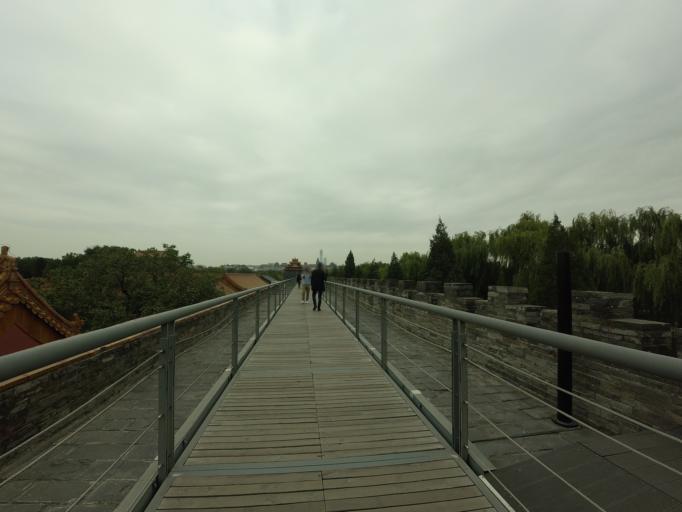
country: CN
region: Beijing
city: Beijing
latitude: 39.9125
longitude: 116.3922
